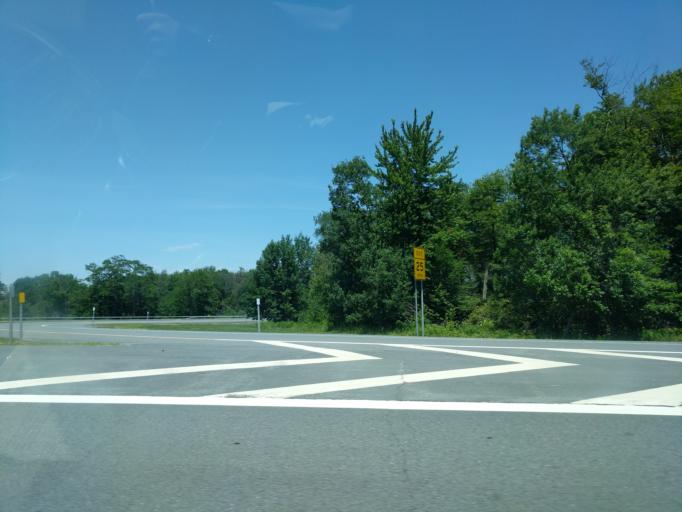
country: US
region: New York
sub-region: Sullivan County
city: Monticello
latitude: 41.6636
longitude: -74.6785
